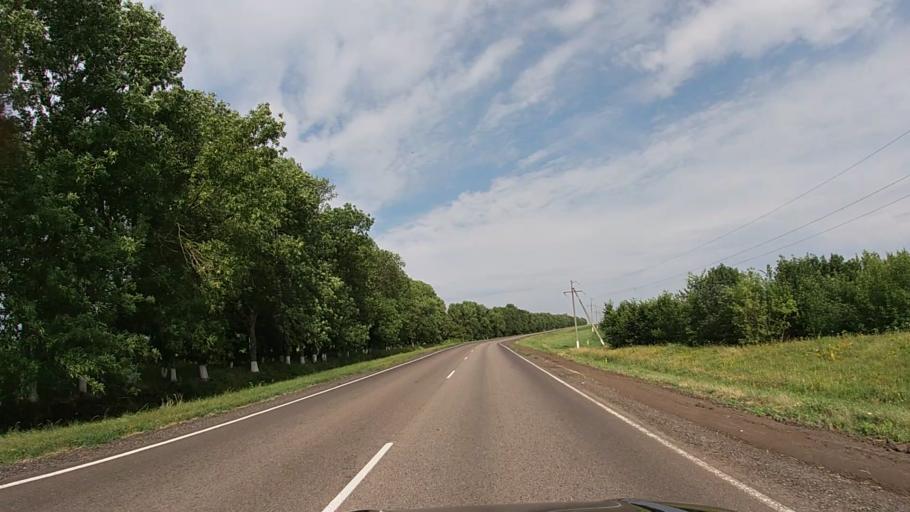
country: RU
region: Belgorod
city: Krasnaya Yaruga
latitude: 50.8018
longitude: 35.5582
